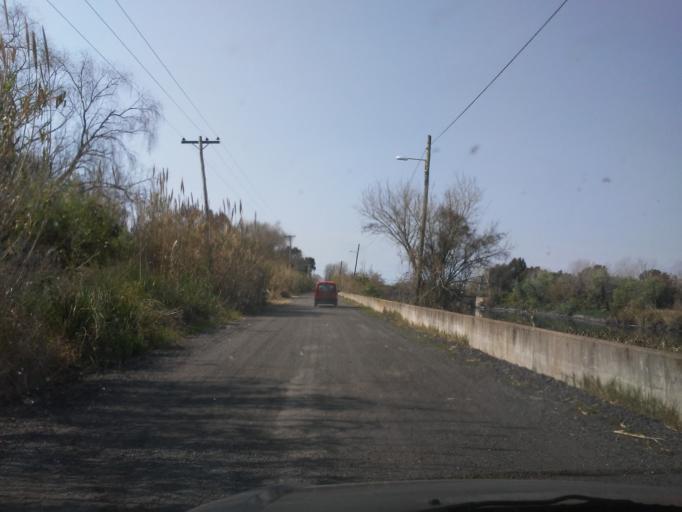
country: AR
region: Buenos Aires
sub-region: Partido de Avellaneda
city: Avellaneda
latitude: -34.6737
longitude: -58.3075
